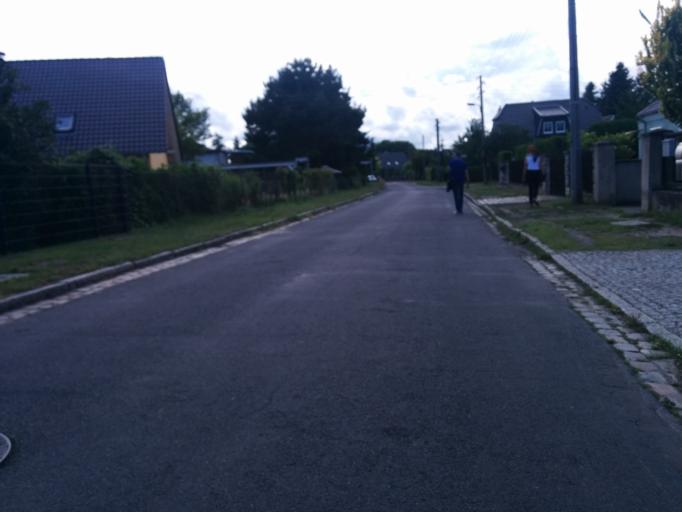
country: DE
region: Berlin
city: Biesdorf
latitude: 52.4840
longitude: 13.5713
